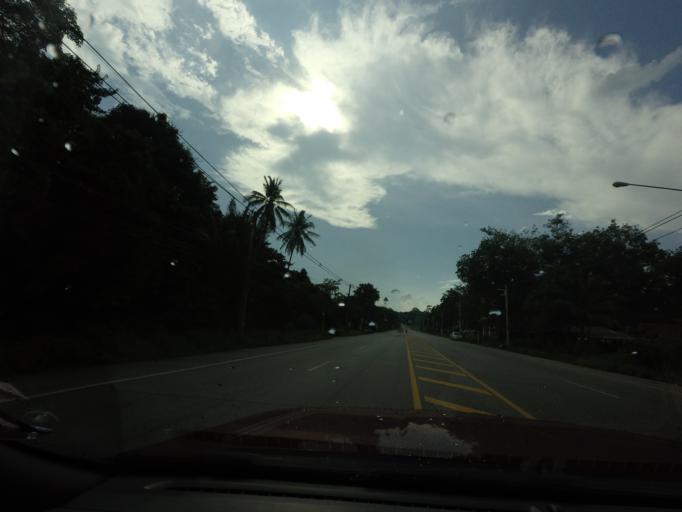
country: TH
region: Pattani
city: Mae Lan
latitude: 6.6641
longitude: 101.1650
